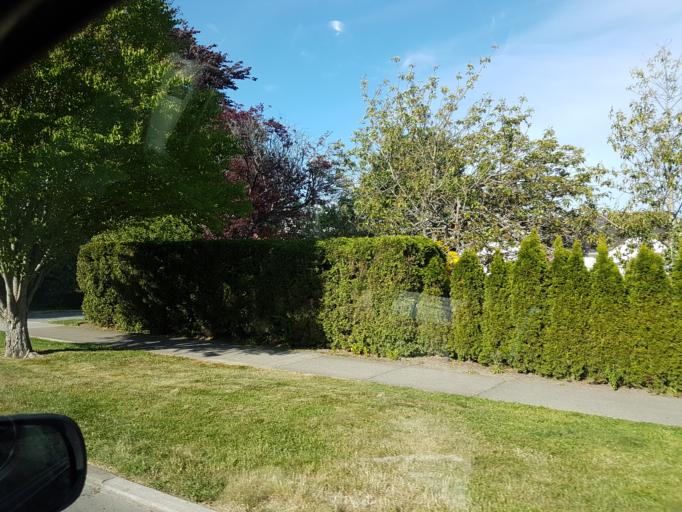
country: CA
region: British Columbia
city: Oak Bay
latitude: 48.4471
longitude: -123.2944
